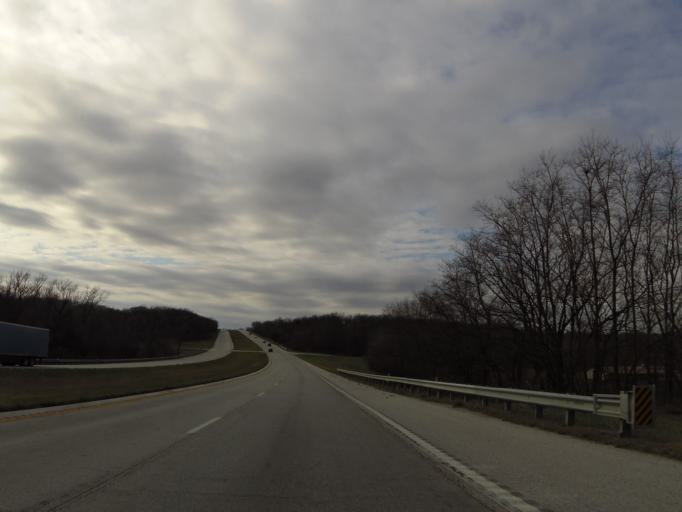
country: US
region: Missouri
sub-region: Marion County
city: Hannibal
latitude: 39.7438
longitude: -91.4272
